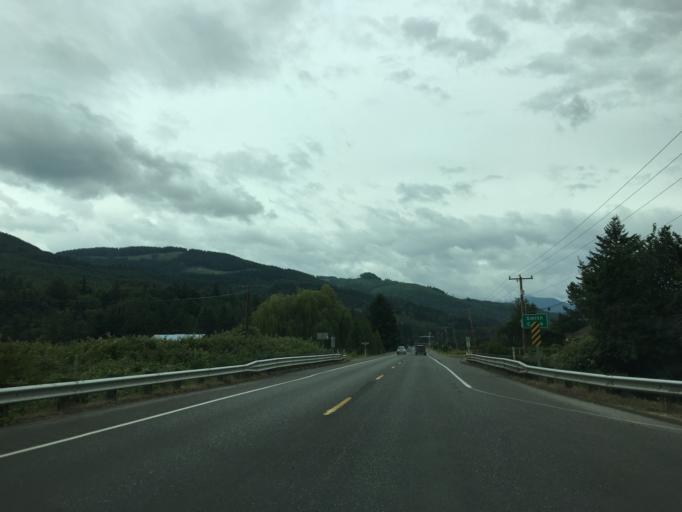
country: US
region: Washington
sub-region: Whatcom County
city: Nooksack
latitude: 48.8435
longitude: -122.2758
